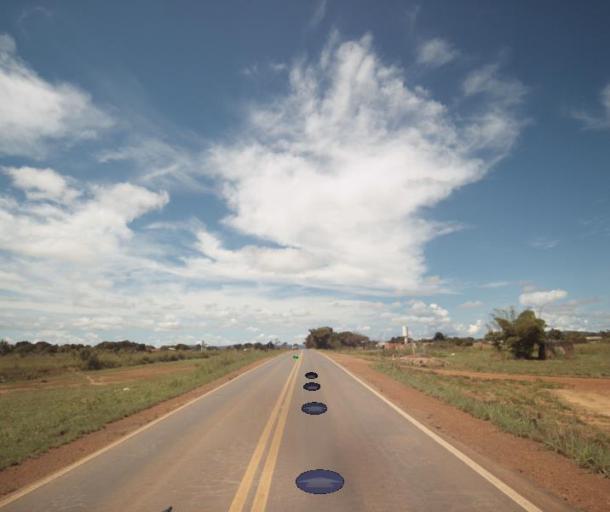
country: BR
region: Goias
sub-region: Padre Bernardo
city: Padre Bernardo
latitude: -15.3561
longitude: -48.2293
